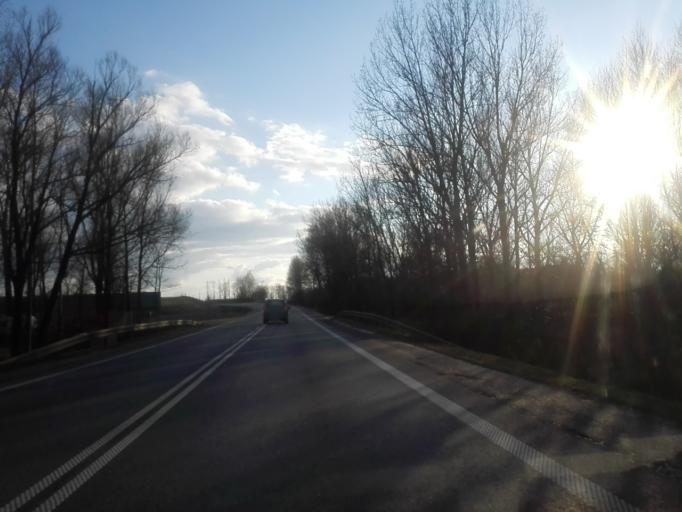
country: PL
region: Podlasie
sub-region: Suwalki
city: Suwalki
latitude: 54.1962
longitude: 23.0157
